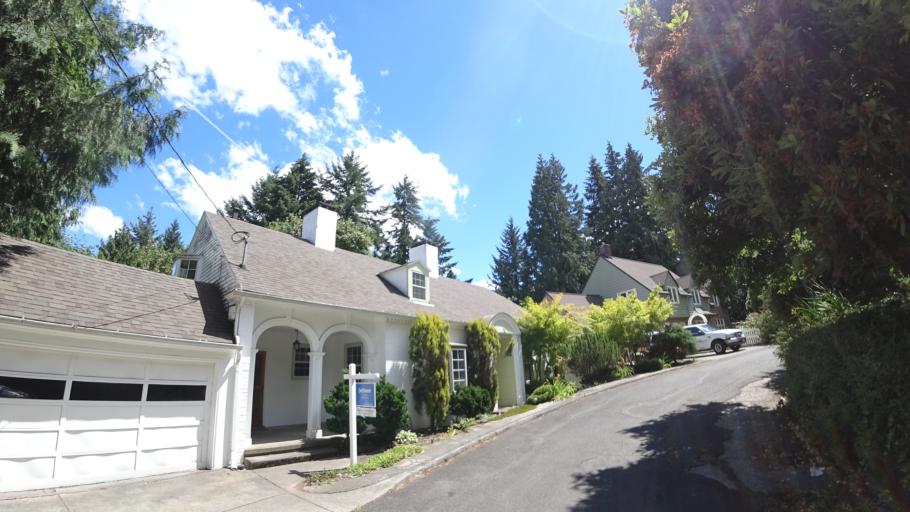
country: US
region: Oregon
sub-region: Multnomah County
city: Portland
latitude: 45.5043
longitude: -122.6983
